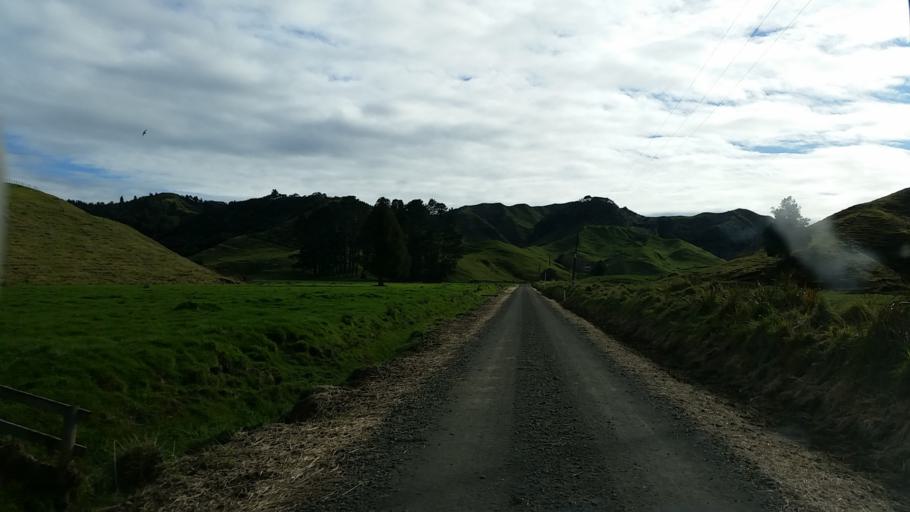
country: NZ
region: Taranaki
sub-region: South Taranaki District
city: Eltham
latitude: -39.2286
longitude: 174.5648
